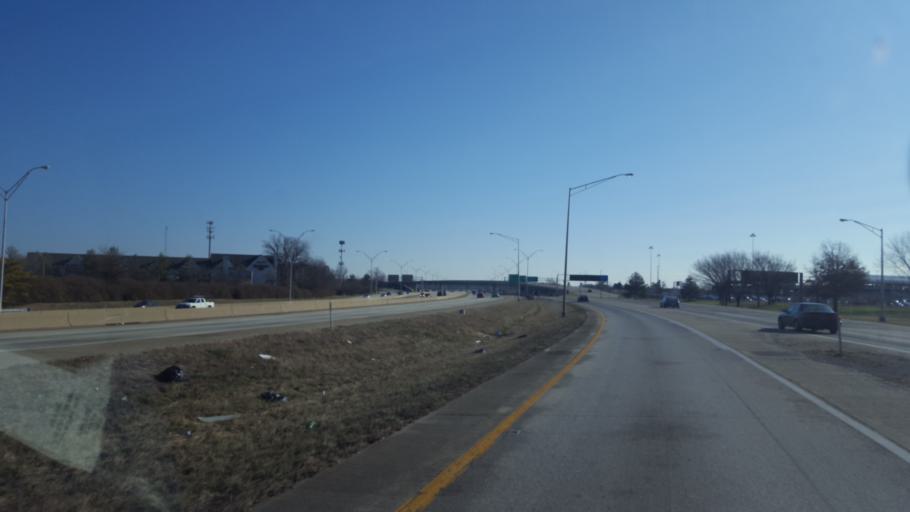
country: US
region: Kentucky
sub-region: Jefferson County
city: Audubon Park
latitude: 38.1892
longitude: -85.7467
